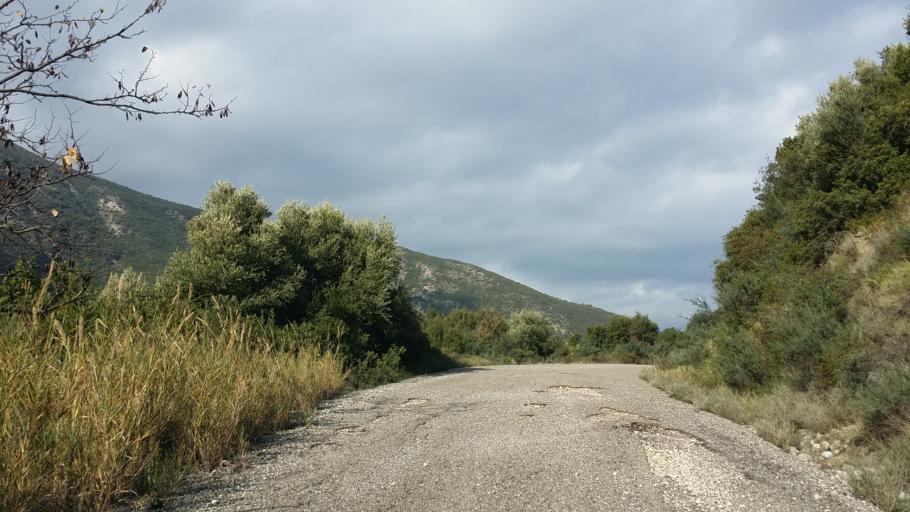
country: GR
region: West Greece
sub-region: Nomos Aitolias kai Akarnanias
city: Katouna
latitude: 38.8451
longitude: 21.0496
